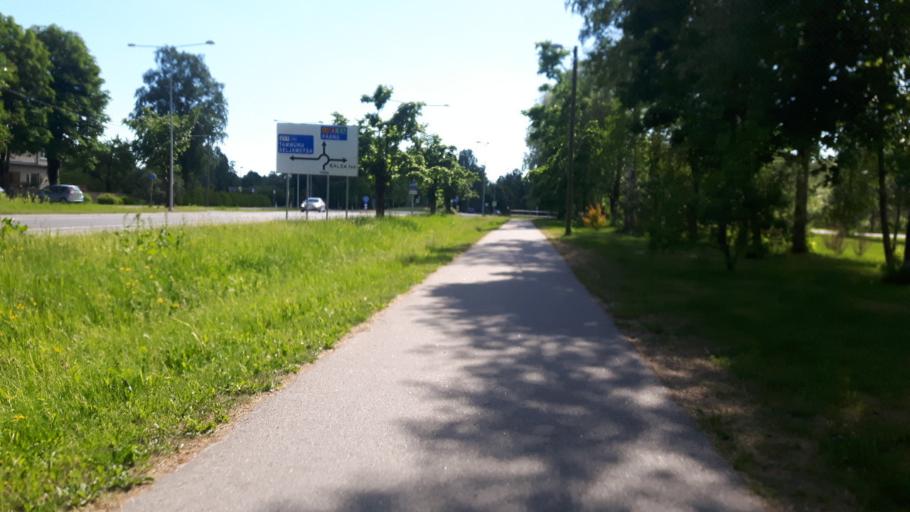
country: EE
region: Paernumaa
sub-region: Paikuse vald
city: Paikuse
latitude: 58.3768
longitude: 24.6241
